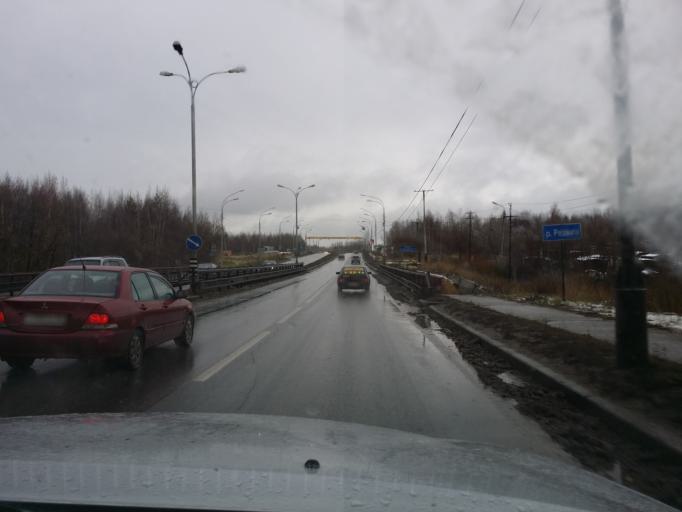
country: RU
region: Khanty-Mansiyskiy Avtonomnyy Okrug
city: Nizhnevartovsk
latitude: 60.9715
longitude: 76.5269
